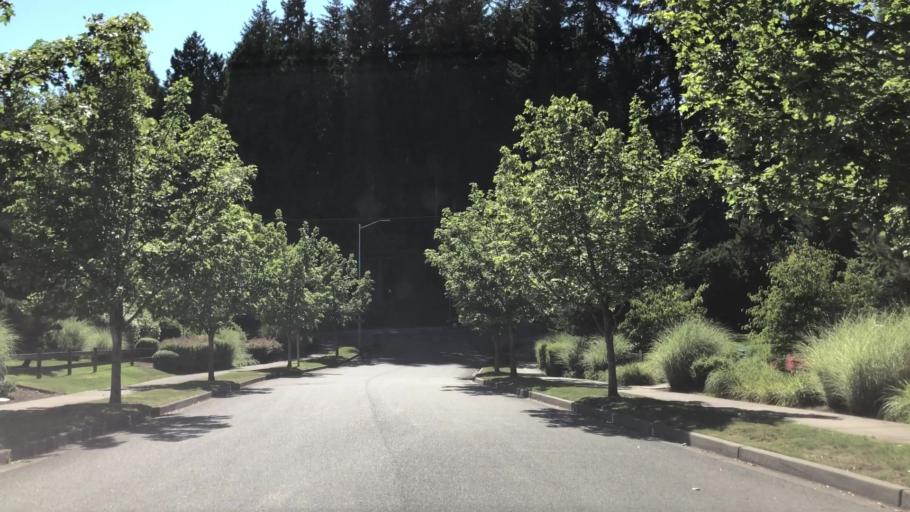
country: US
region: Washington
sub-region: Snohomish County
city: North Creek
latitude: 47.7891
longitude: -122.1855
